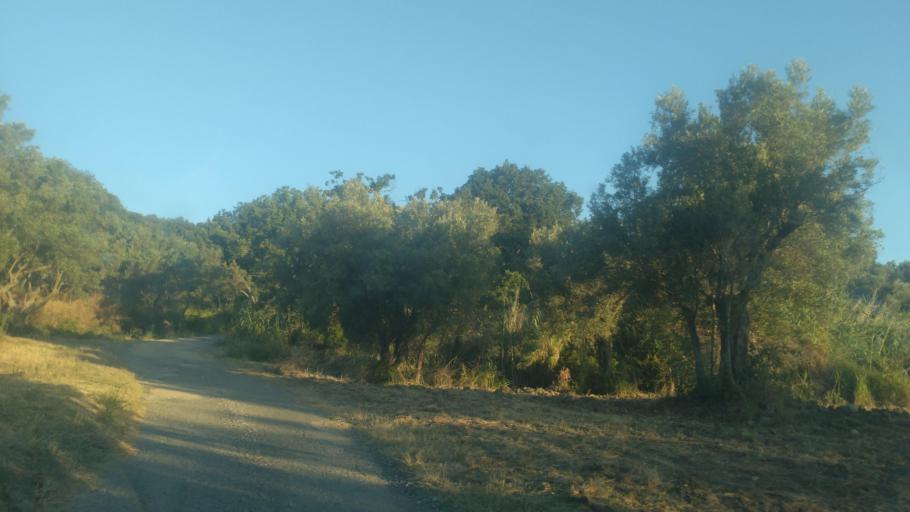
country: IT
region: Calabria
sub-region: Provincia di Catanzaro
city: Staletti
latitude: 38.7737
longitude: 16.5473
